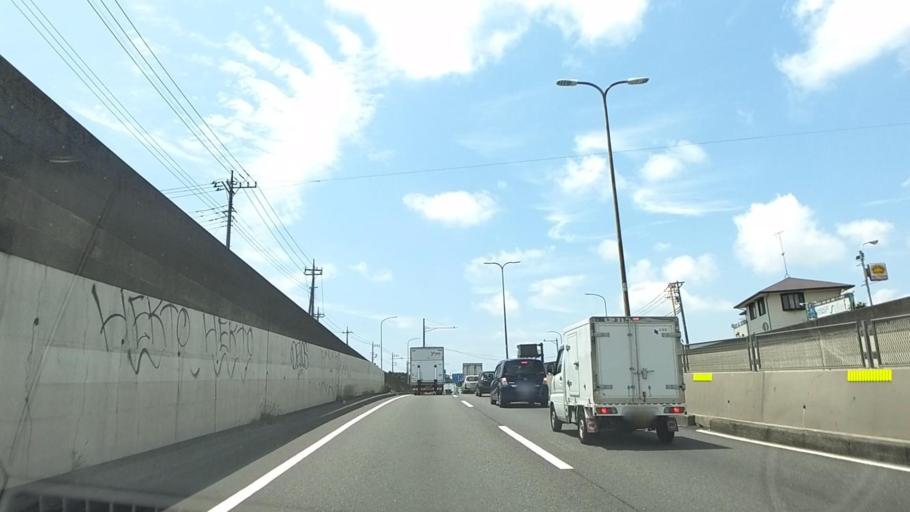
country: JP
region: Kanagawa
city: Minami-rinkan
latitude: 35.4854
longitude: 139.4610
